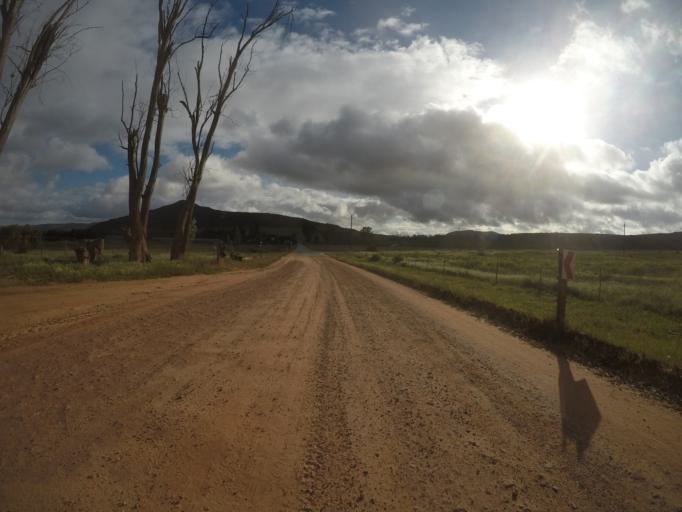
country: ZA
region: Western Cape
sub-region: West Coast District Municipality
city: Clanwilliam
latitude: -32.3430
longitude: 18.8365
